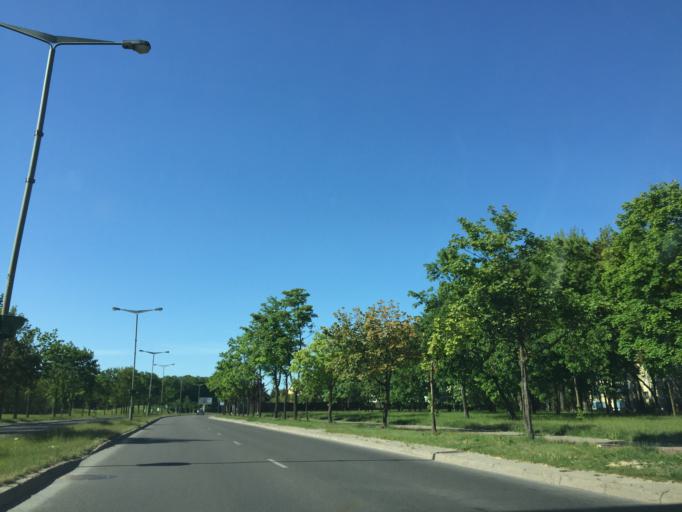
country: LT
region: Panevezys
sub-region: Panevezys City
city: Panevezys
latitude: 55.7364
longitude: 24.3393
